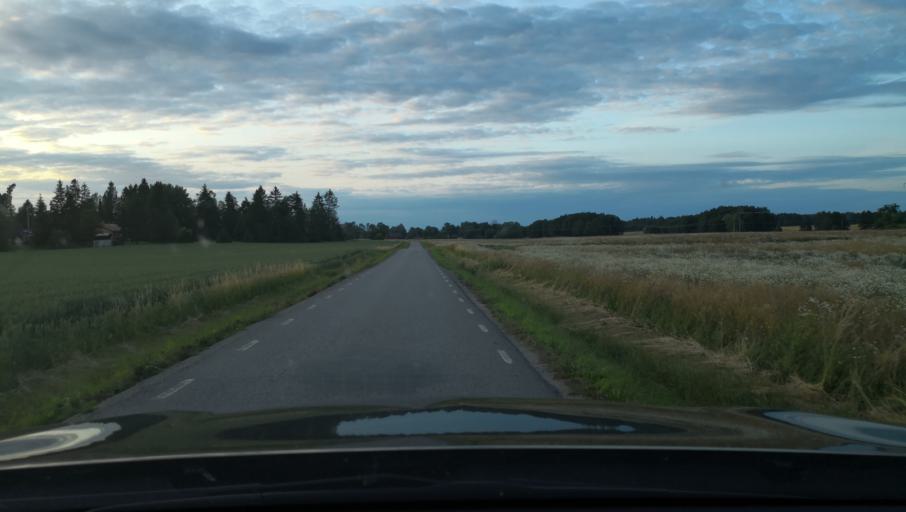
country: SE
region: Uppsala
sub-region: Uppsala Kommun
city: Vattholma
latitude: 60.0289
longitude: 17.6644
